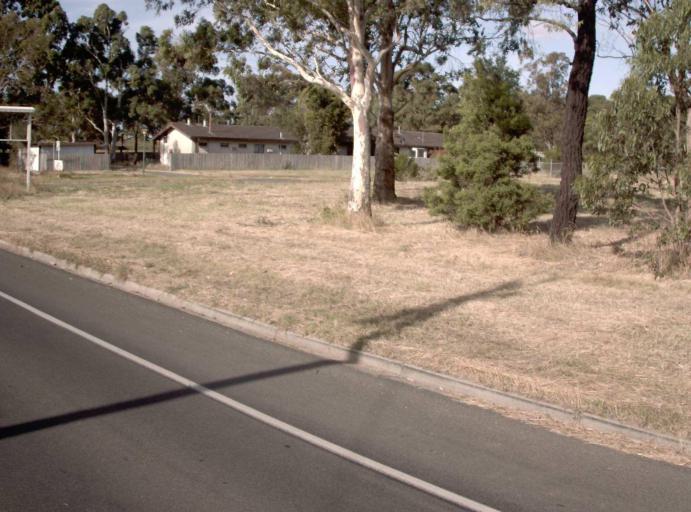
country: AU
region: Victoria
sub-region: Latrobe
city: Traralgon
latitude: -38.2065
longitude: 146.5208
